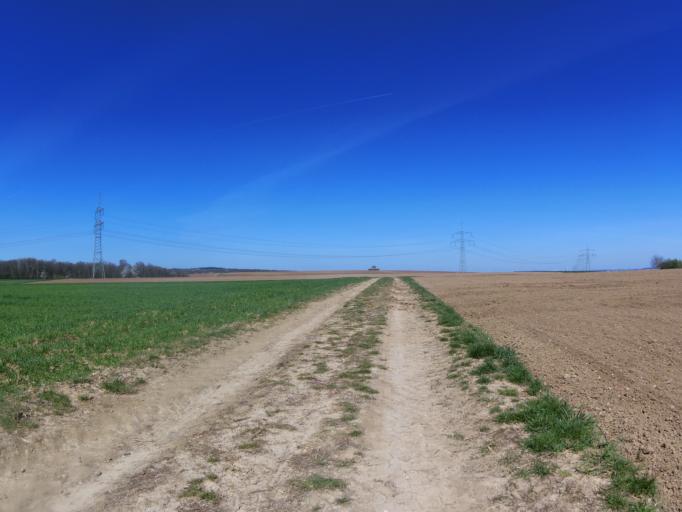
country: DE
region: Bavaria
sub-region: Regierungsbezirk Unterfranken
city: Biebelried
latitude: 49.8063
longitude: 10.0788
